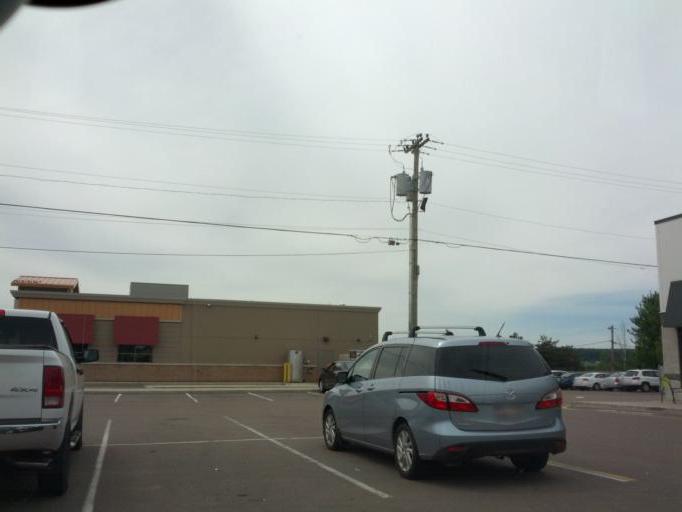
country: CA
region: New Brunswick
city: Moncton
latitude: 46.1229
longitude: -64.8519
